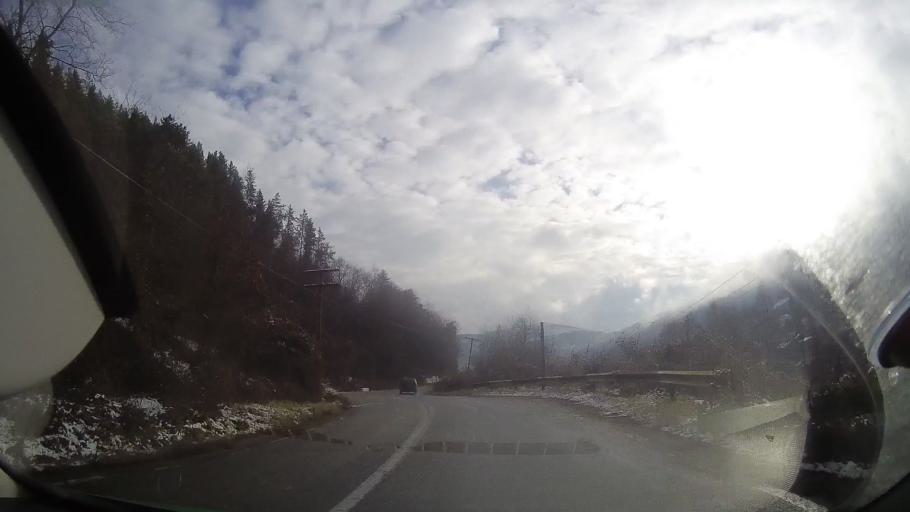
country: RO
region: Alba
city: Salciua de Sus
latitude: 46.3964
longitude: 23.3846
